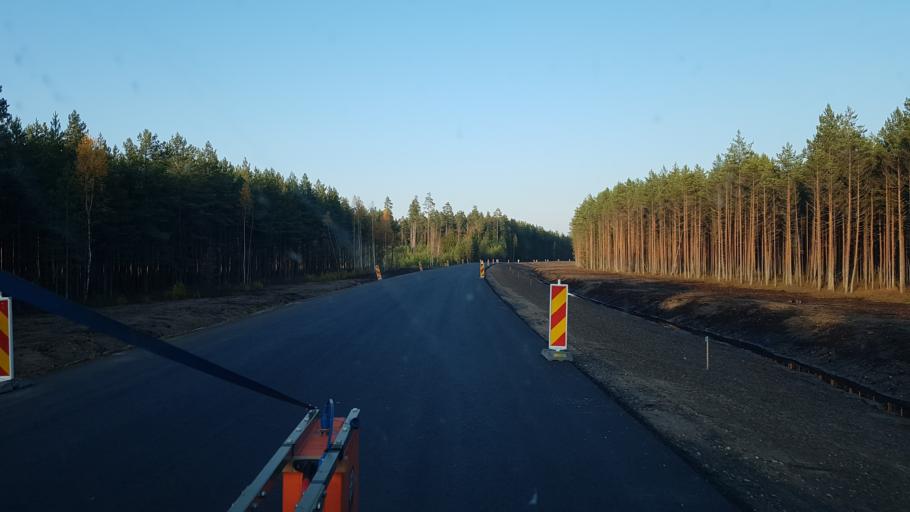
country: EE
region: Polvamaa
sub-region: Polva linn
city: Polva
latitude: 57.9316
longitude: 27.1849
